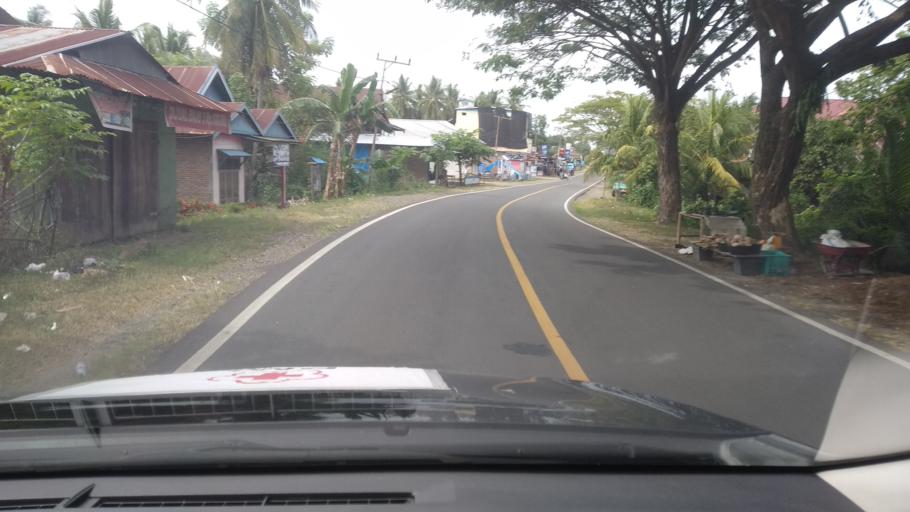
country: ID
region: Sulawesi Barat
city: Malunda
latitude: -3.0081
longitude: 118.8566
